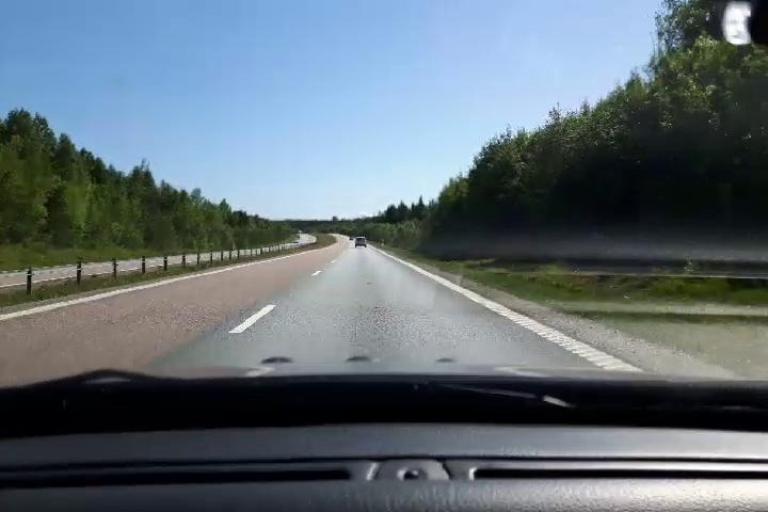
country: SE
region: Gaevleborg
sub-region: Hudiksvalls Kommun
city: Iggesund
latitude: 61.4970
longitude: 16.9847
